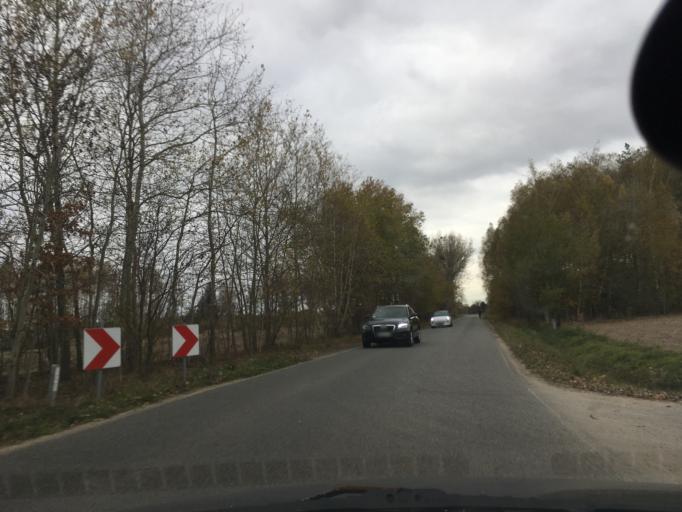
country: PL
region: Lodz Voivodeship
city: Zabia Wola
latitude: 52.0196
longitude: 20.7228
